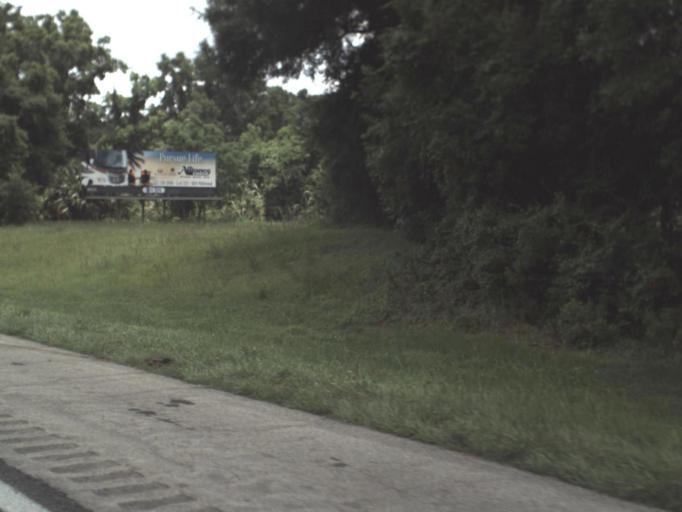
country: US
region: Florida
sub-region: Alachua County
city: Gainesville
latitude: 29.5362
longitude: -82.3243
